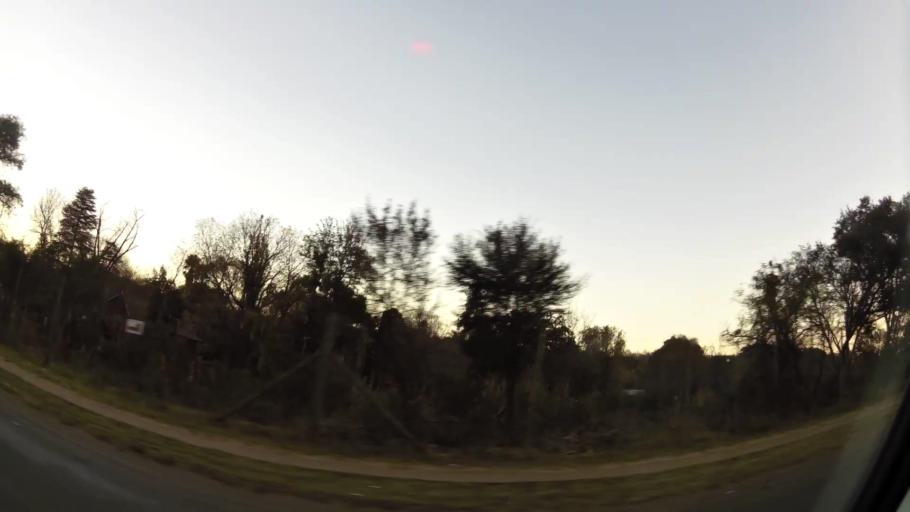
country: ZA
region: Gauteng
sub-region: City of Tshwane Metropolitan Municipality
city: Pretoria
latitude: -25.7424
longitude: 28.3020
